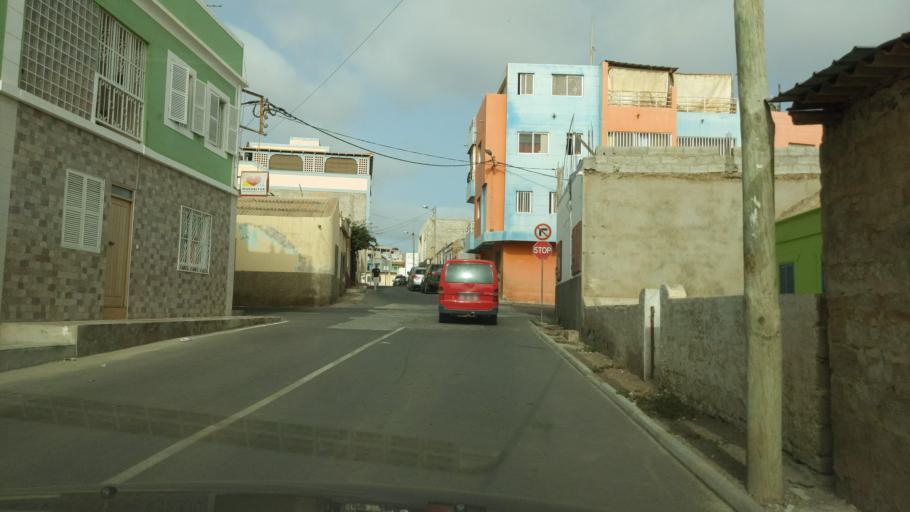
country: CV
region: Sal
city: Espargos
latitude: 16.7560
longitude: -22.9457
